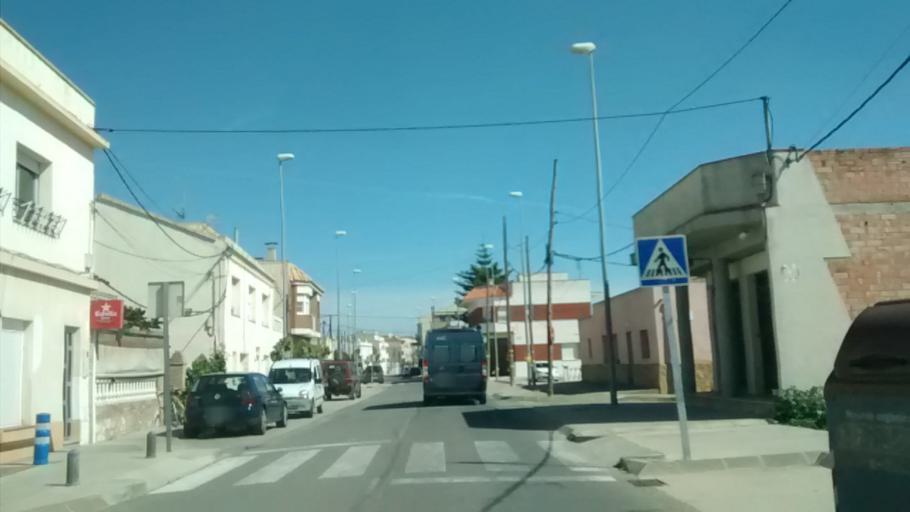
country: ES
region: Catalonia
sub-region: Provincia de Tarragona
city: Deltebre
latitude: 40.7154
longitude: 0.7463
